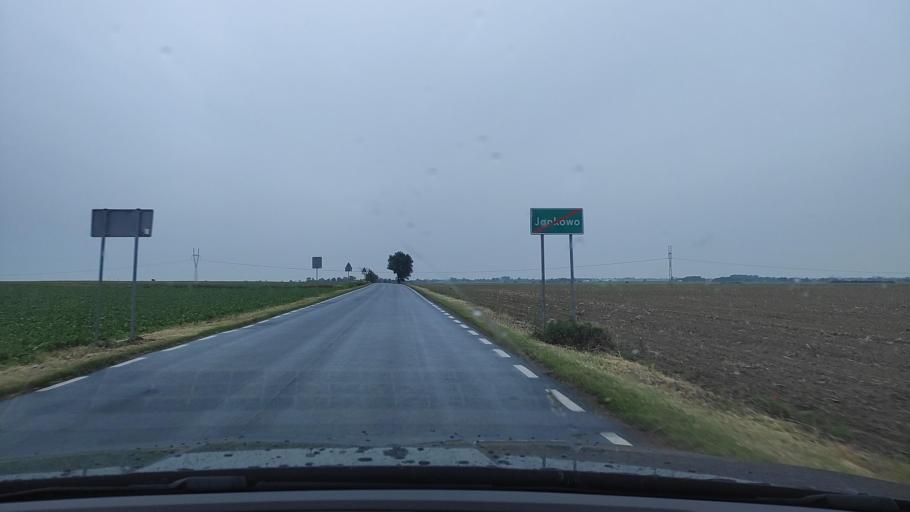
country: PL
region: Greater Poland Voivodeship
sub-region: Powiat poznanski
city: Kostrzyn
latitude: 52.4424
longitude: 17.1695
